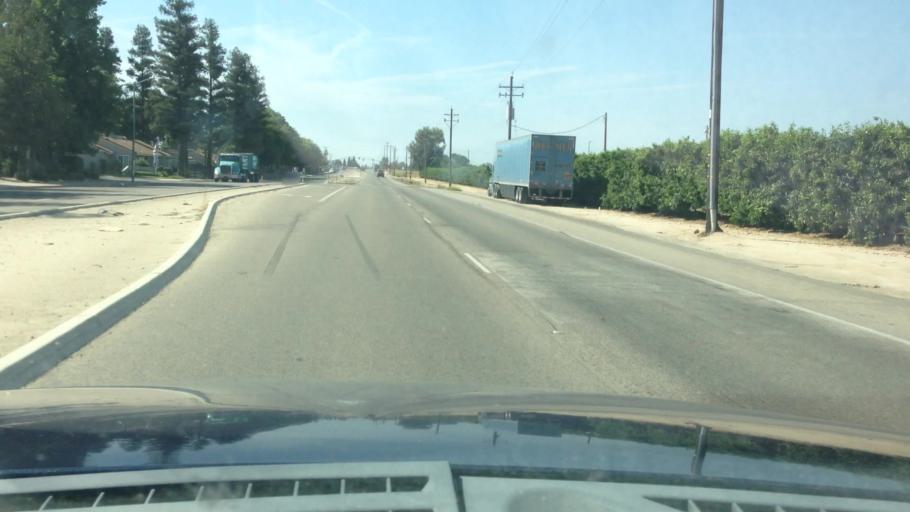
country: US
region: California
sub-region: Fresno County
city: Parlier
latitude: 36.6105
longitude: -119.5568
